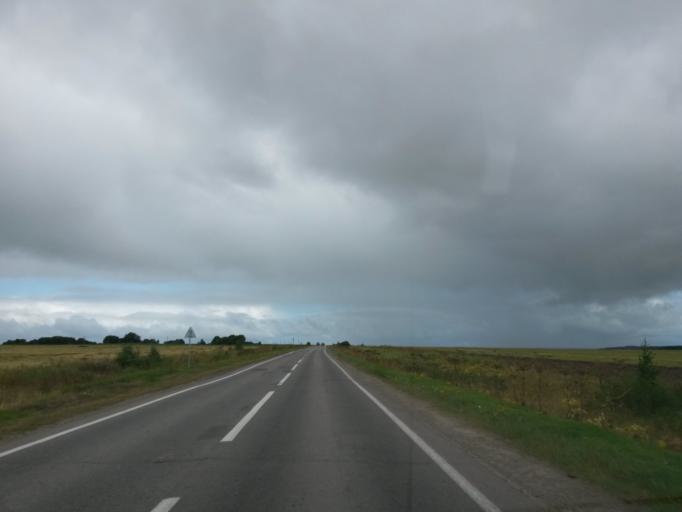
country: RU
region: Jaroslavl
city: Yaroslavl
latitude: 57.7525
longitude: 39.8753
